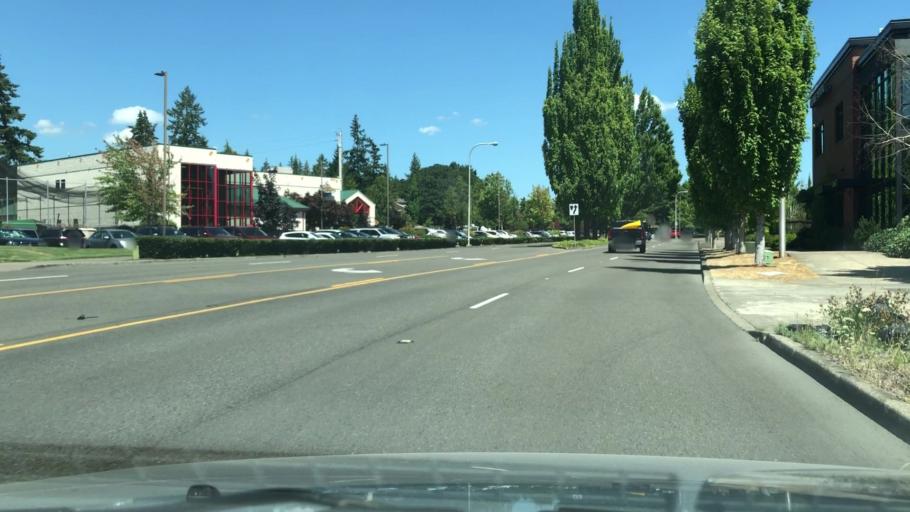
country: US
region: Oregon
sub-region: Clackamas County
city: Wilsonville
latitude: 45.3088
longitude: -122.7677
